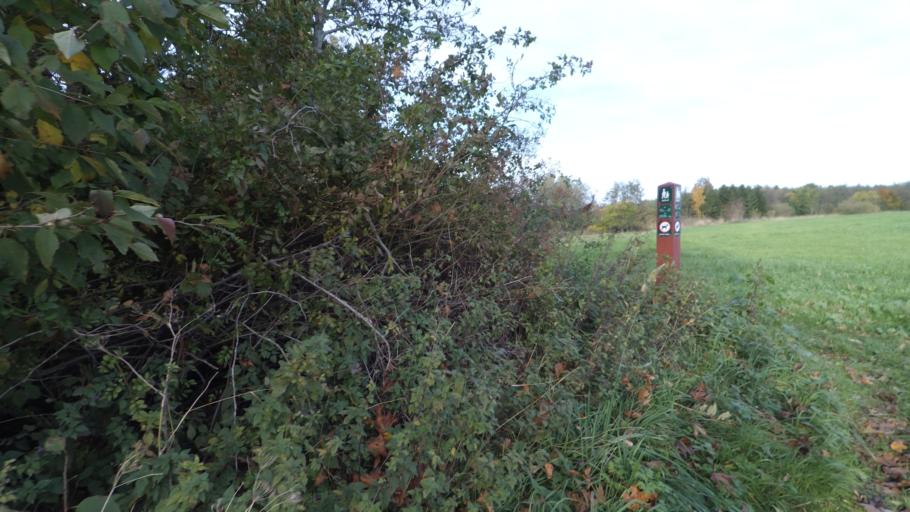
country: DK
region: Central Jutland
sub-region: Arhus Kommune
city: Framlev
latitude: 56.1338
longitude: 10.0226
